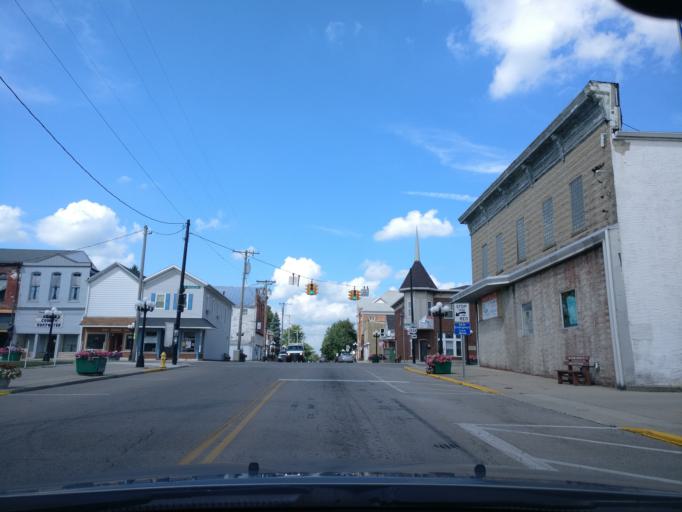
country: US
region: Ohio
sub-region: Greene County
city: Jamestown
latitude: 39.6578
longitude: -83.7349
